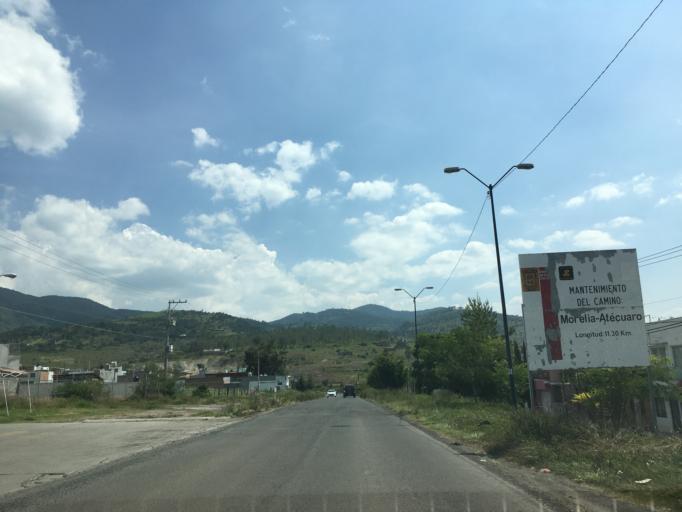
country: MX
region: Michoacan
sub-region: Morelia
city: Morelos
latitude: 19.6550
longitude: -101.2025
